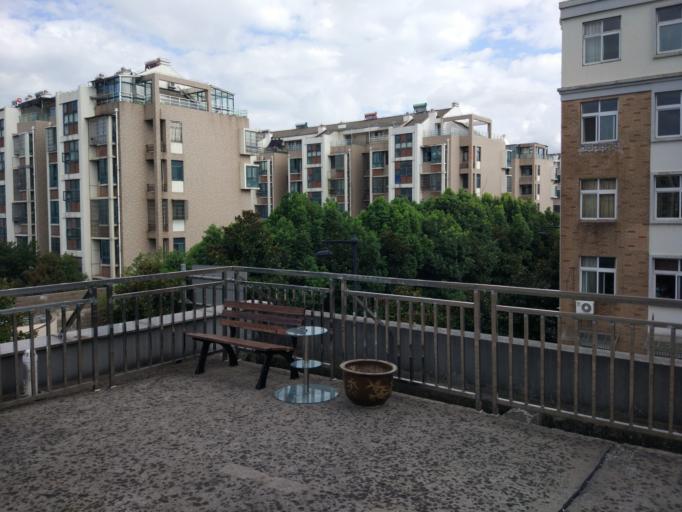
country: CN
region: Zhejiang Sheng
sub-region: Ningbo Shi
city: Yuyao
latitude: 30.0681
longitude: 121.1827
